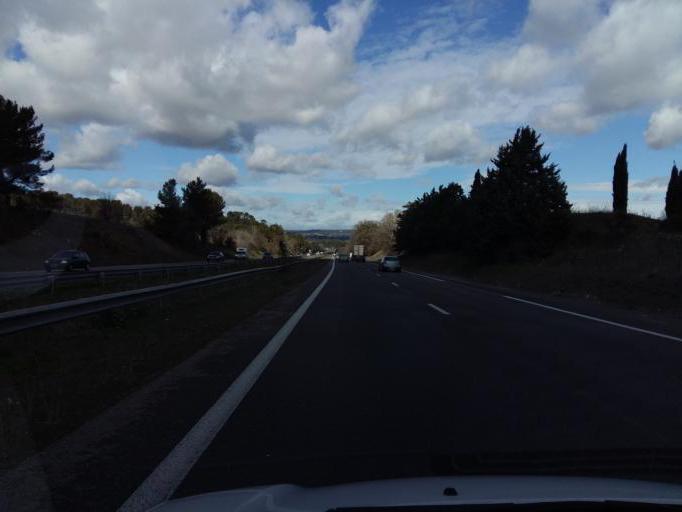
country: FR
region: Provence-Alpes-Cote d'Azur
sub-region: Departement des Bouches-du-Rhone
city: Bouc-Bel-Air
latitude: 43.4817
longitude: 5.4085
